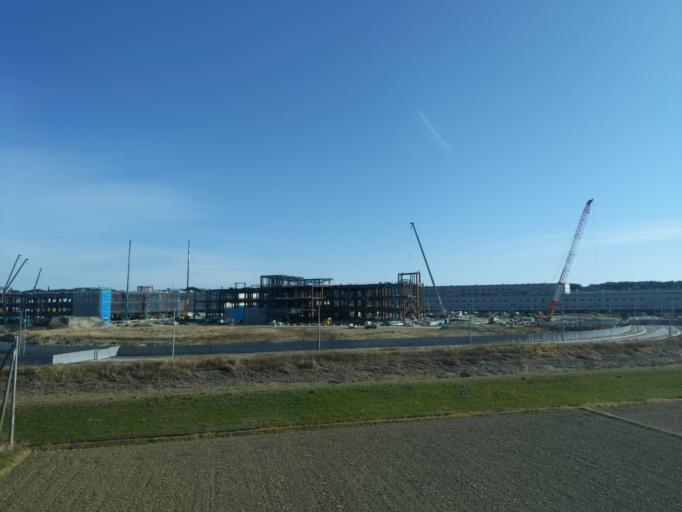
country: JP
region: Miyagi
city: Rifu
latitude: 38.3221
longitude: 140.9685
